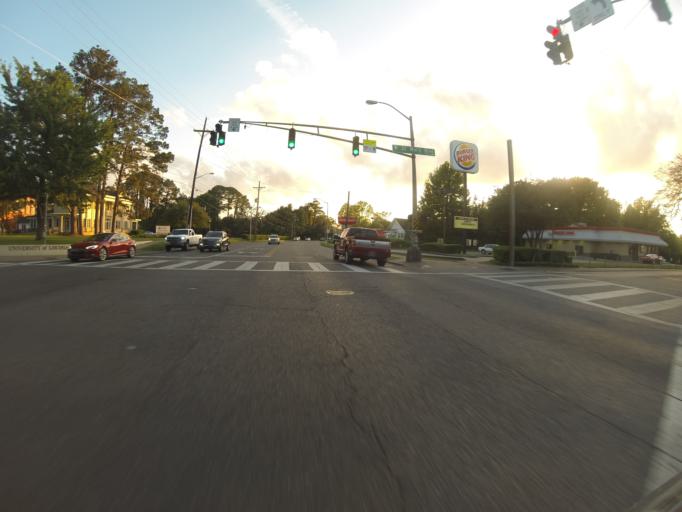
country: US
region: Louisiana
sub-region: Lafayette Parish
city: Lafayette
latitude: 30.2149
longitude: -92.0214
